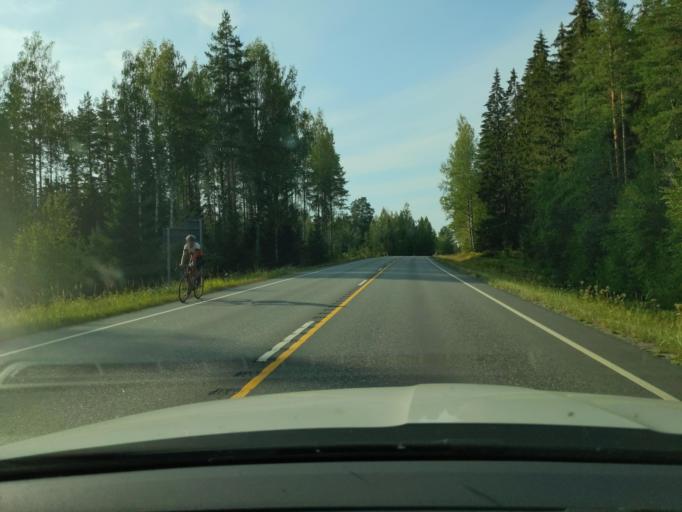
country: FI
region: Paijanne Tavastia
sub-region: Lahti
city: Padasjoki
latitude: 61.3070
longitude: 25.2941
